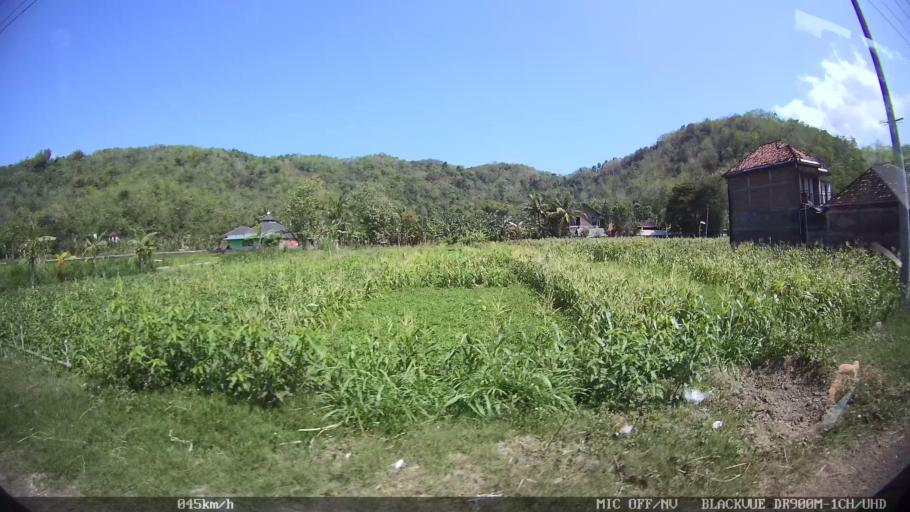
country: ID
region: Daerah Istimewa Yogyakarta
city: Pundong
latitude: -7.9571
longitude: 110.3697
